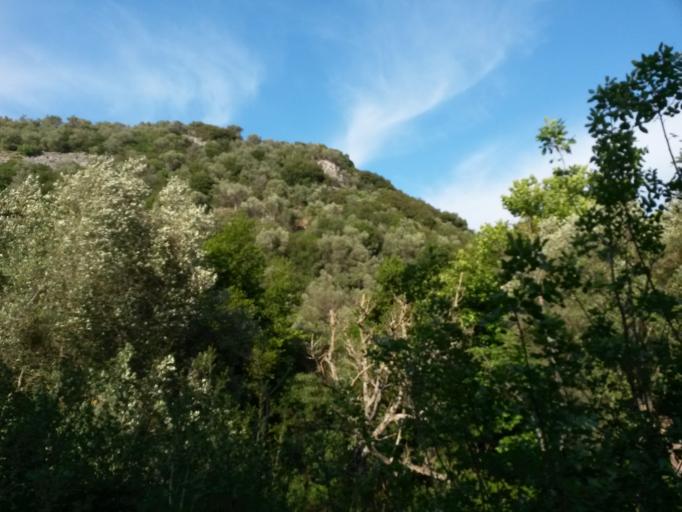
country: GR
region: North Aegean
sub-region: Nomos Lesvou
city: Agiasos
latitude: 39.1121
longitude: 26.3915
